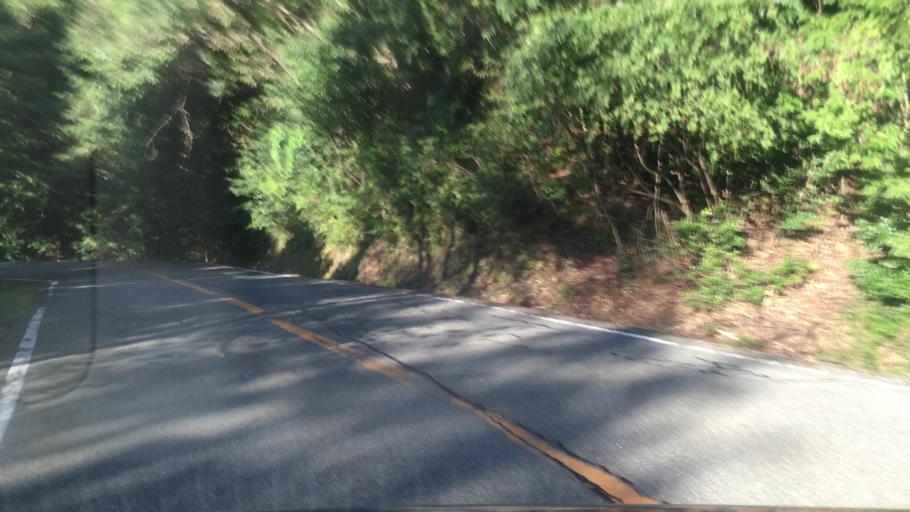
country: JP
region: Hyogo
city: Toyooka
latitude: 35.6199
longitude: 134.8721
